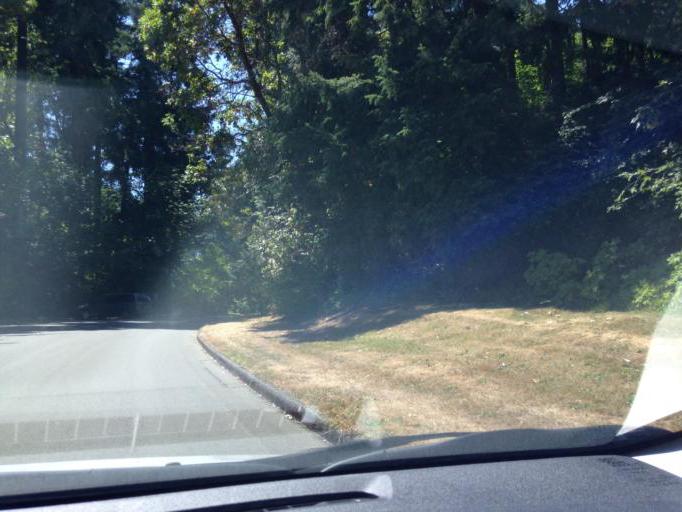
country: US
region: Washington
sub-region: King County
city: Mercer Island
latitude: 47.5513
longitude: -122.2518
